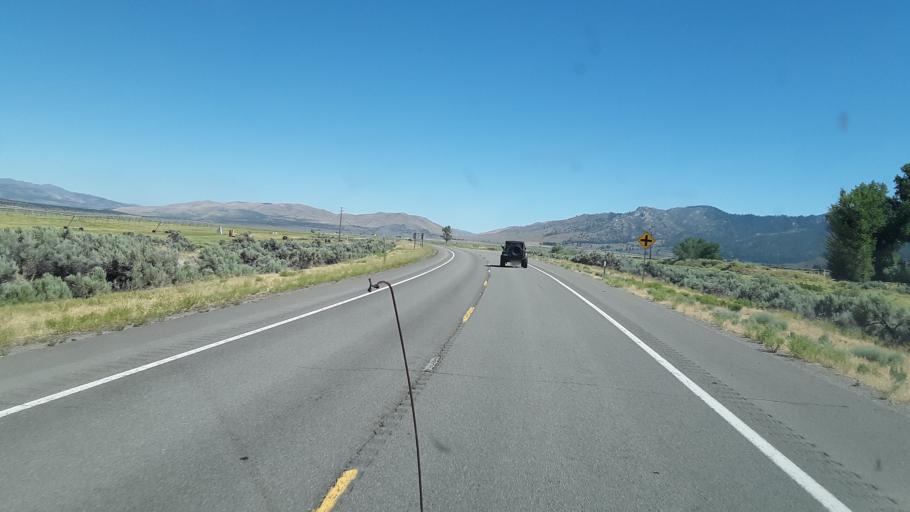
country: US
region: Nevada
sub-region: Washoe County
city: Cold Springs
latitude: 40.0010
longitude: -120.0816
